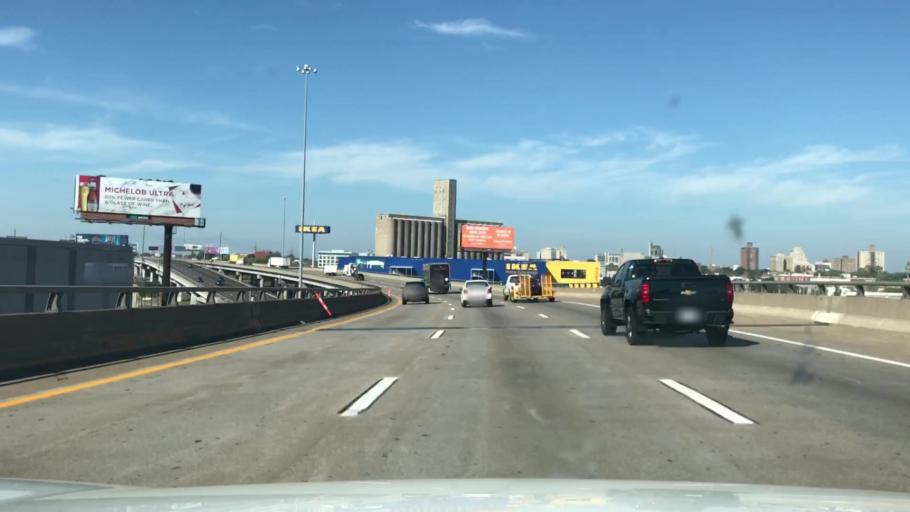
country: US
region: Missouri
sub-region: City of Saint Louis
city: St. Louis
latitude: 38.6325
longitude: -90.2395
